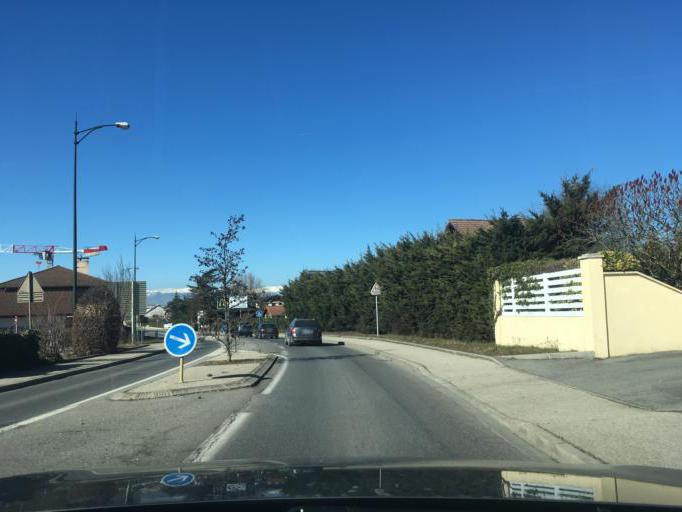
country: FR
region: Rhone-Alpes
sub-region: Departement de la Haute-Savoie
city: Vetraz-Monthoux
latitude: 46.1877
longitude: 6.2710
